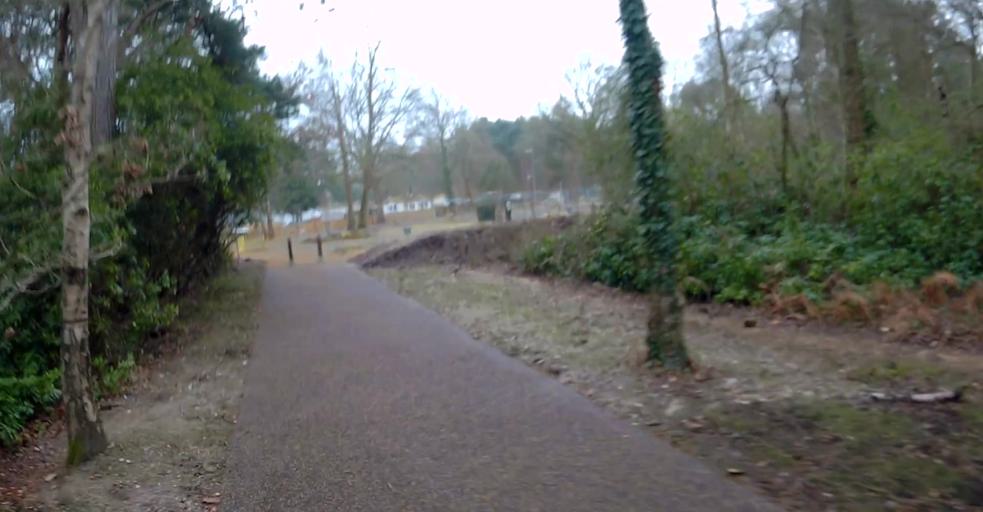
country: GB
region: England
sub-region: Wokingham
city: Barkham
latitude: 51.3788
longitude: -0.8730
